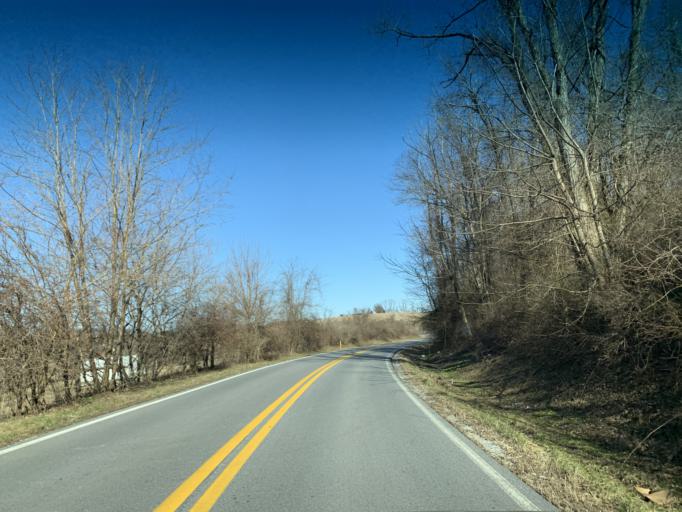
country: US
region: Maryland
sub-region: Carroll County
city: Manchester
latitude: 39.6510
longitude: -76.9595
